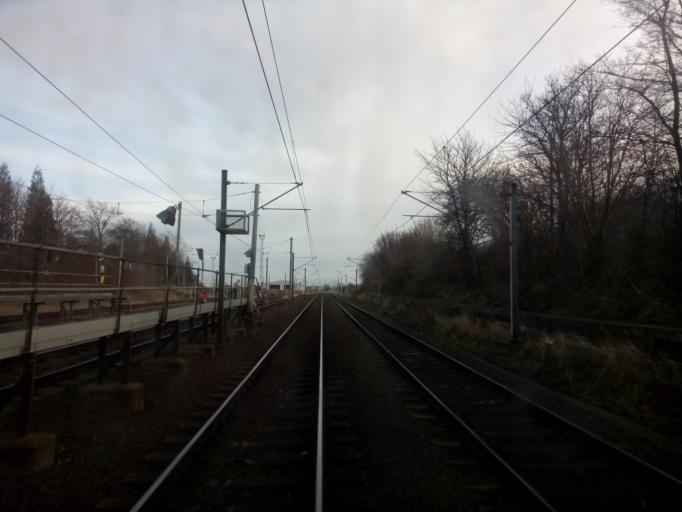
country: GB
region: England
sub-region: Newcastle upon Tyne
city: Gosforth
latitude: 55.0114
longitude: -1.6176
